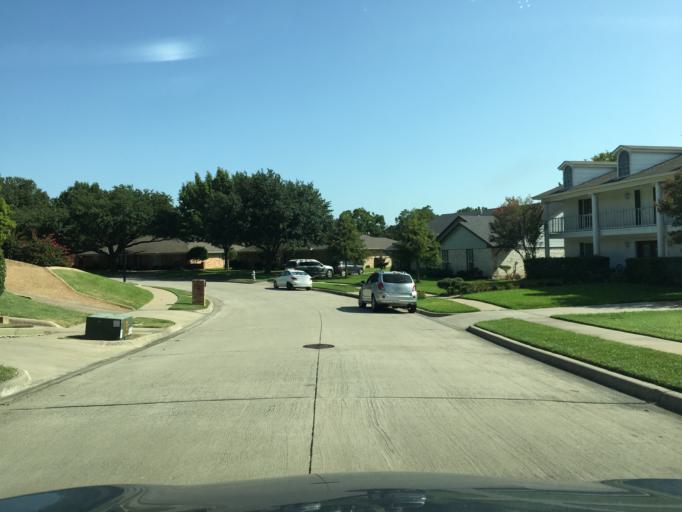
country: US
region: Texas
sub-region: Dallas County
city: Garland
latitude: 32.8772
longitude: -96.6091
